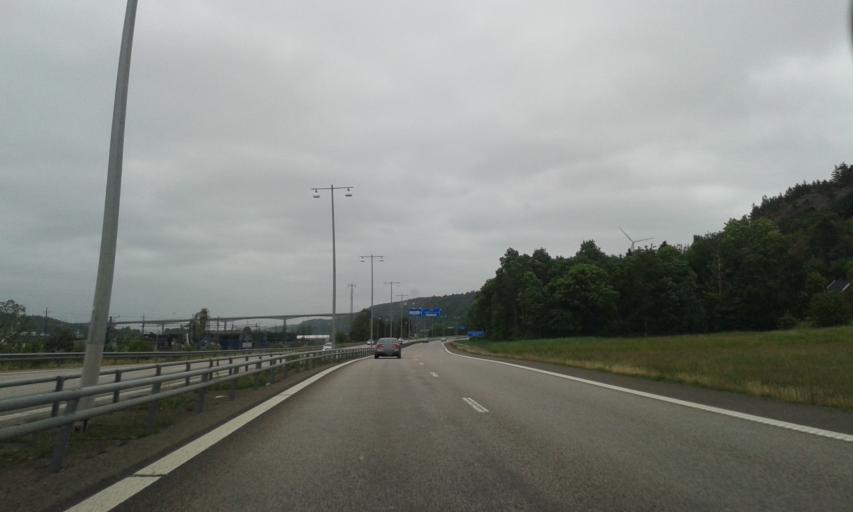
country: SE
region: Vaestra Goetaland
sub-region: Goteborg
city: Hammarkullen
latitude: 57.7822
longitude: 12.0083
